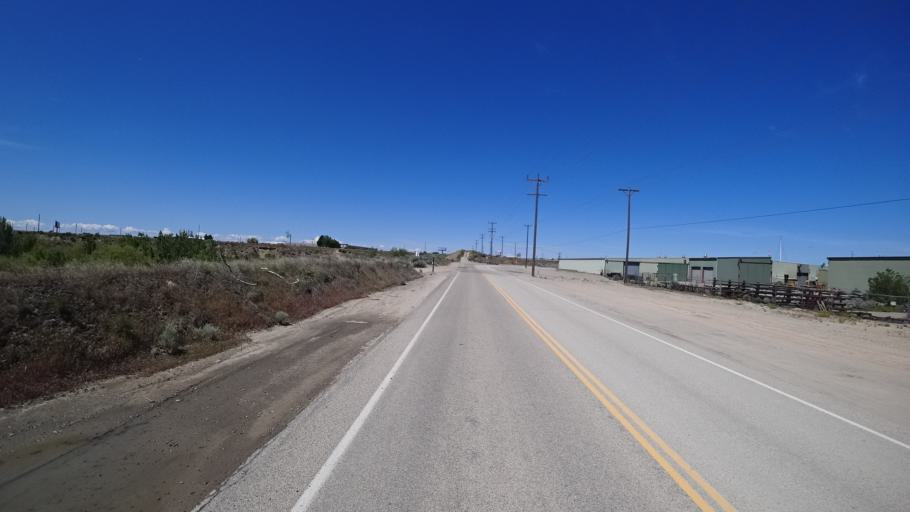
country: US
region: Idaho
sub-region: Ada County
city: Boise
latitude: 43.5604
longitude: -116.1813
